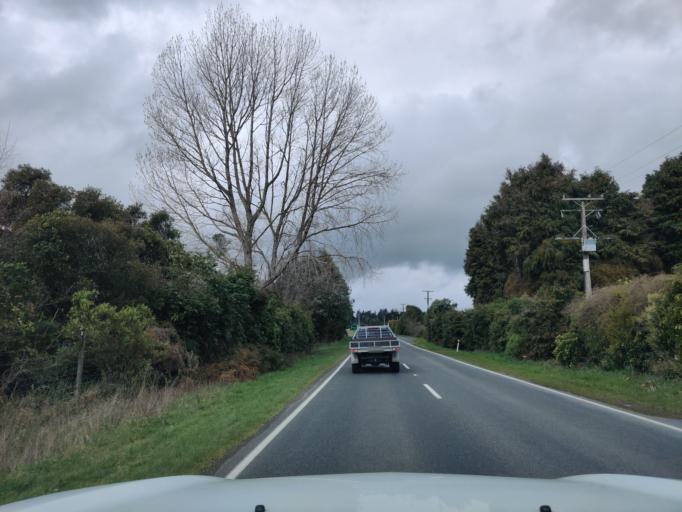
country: NZ
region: Manawatu-Wanganui
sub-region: Ruapehu District
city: Waiouru
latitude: -39.3676
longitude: 175.3191
